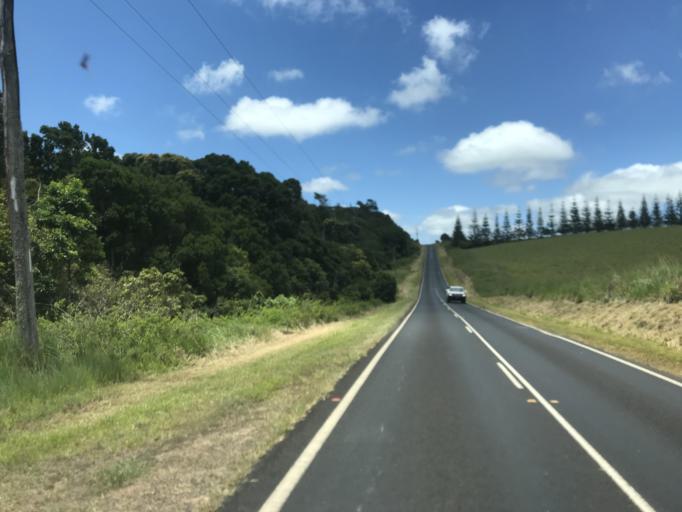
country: AU
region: Queensland
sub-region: Tablelands
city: Ravenshoe
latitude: -17.5018
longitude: 145.4765
